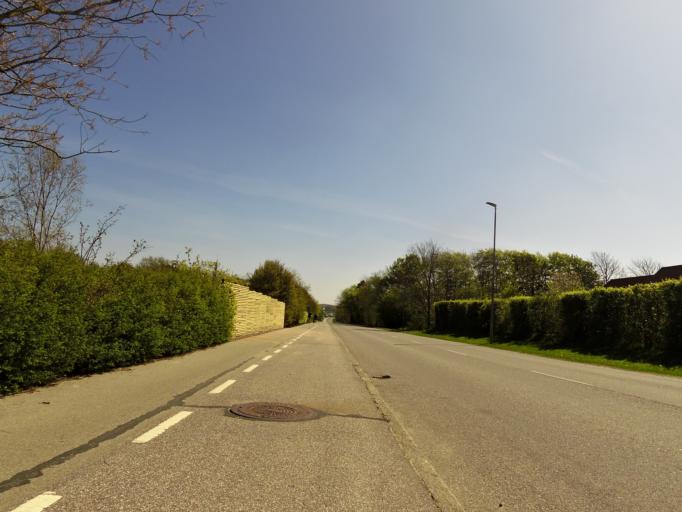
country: DK
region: Central Jutland
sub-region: Struer Kommune
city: Struer
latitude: 56.5083
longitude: 8.5791
